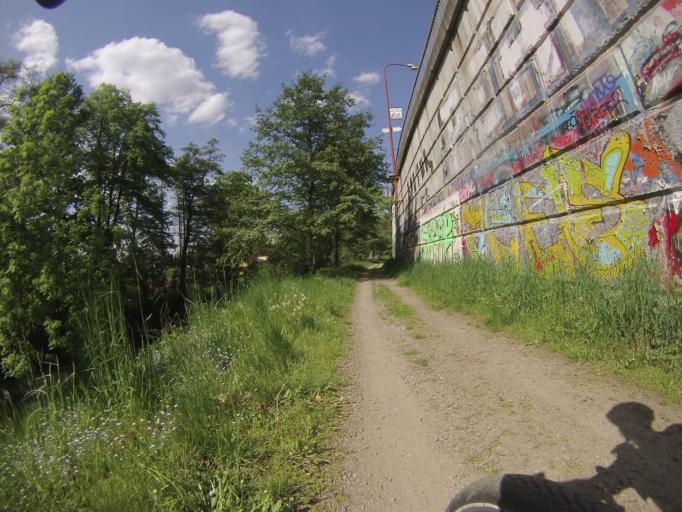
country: CZ
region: South Moravian
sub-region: Okres Blansko
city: Blansko
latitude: 49.3475
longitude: 16.6510
